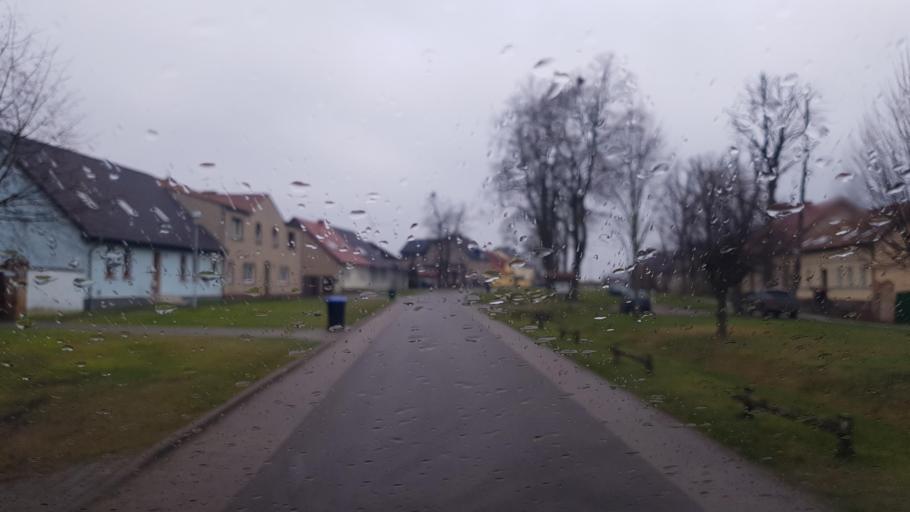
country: DE
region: Brandenburg
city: Zehdenick
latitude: 52.9663
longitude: 13.2825
